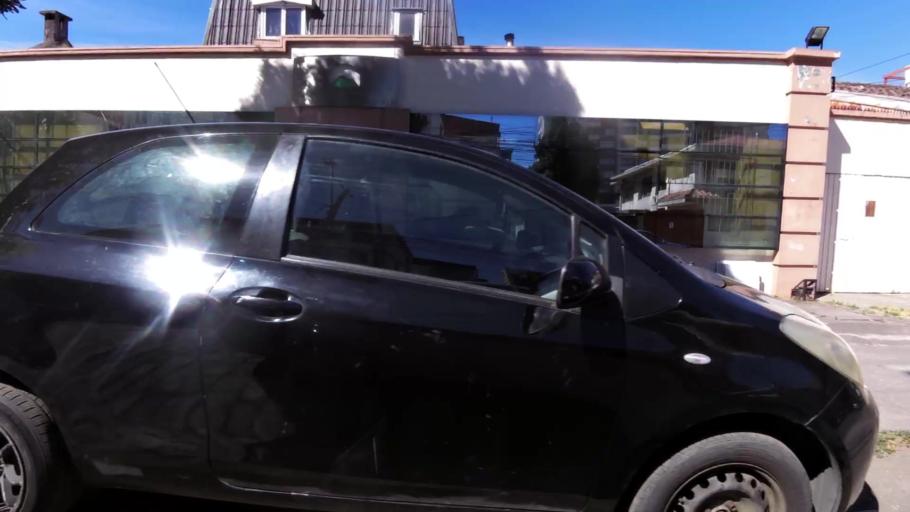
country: CL
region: Biobio
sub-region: Provincia de Concepcion
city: Concepcion
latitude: -36.8195
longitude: -73.0382
